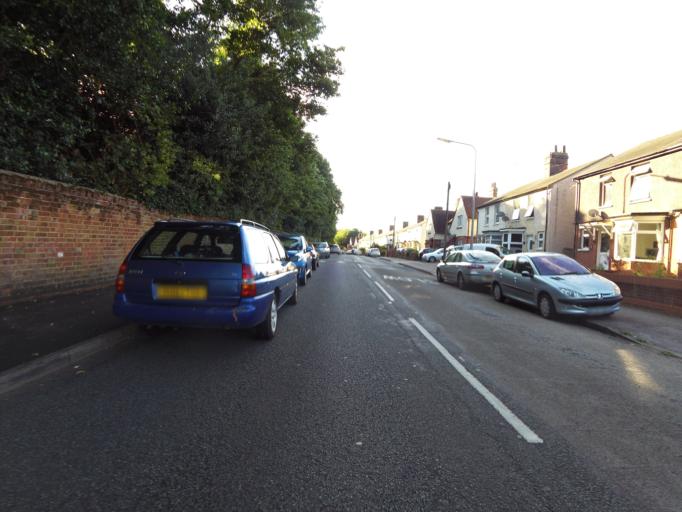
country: GB
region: England
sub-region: Suffolk
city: Ipswich
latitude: 52.0479
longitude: 1.1761
